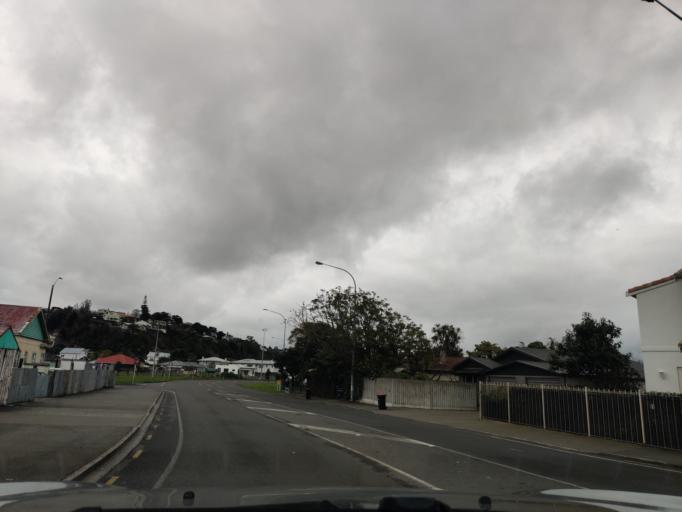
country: NZ
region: Hawke's Bay
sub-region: Napier City
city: Napier
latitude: -39.4783
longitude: 176.9080
